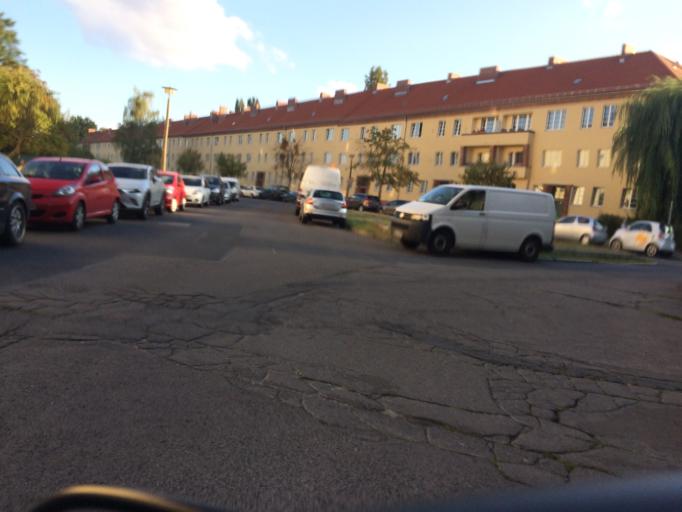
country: DE
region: Berlin
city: Heinersdorf
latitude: 52.5602
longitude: 13.4442
